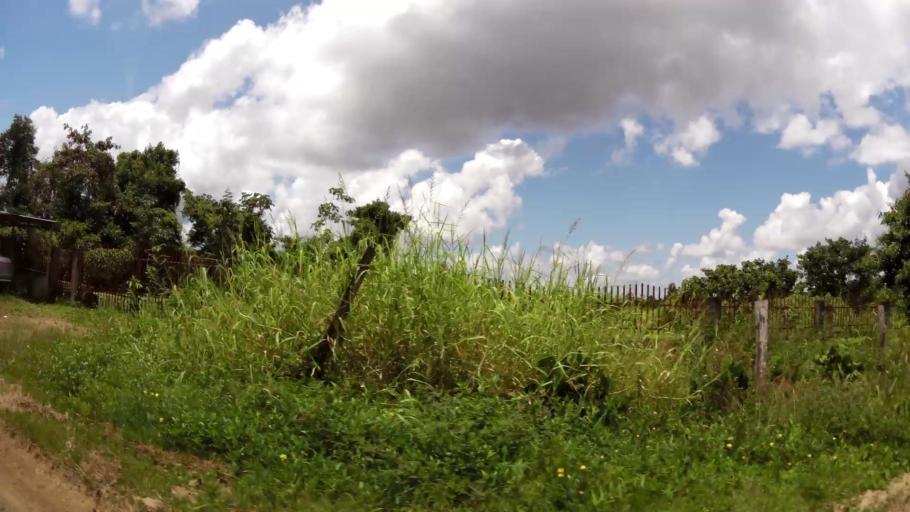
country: SR
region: Paramaribo
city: Paramaribo
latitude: 5.8023
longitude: -55.1318
